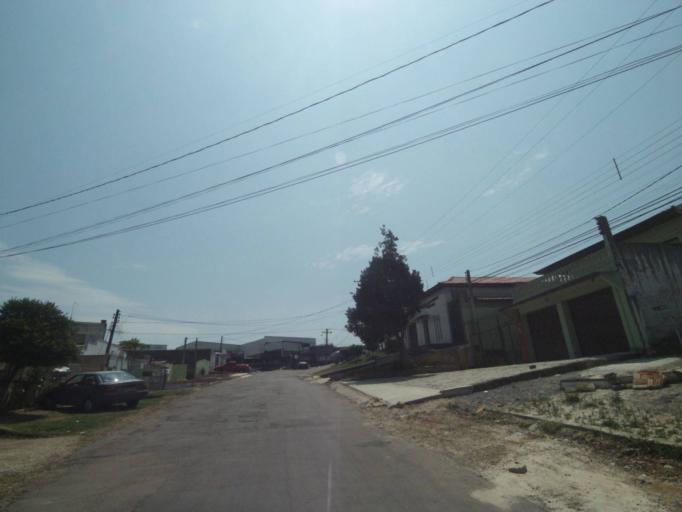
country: BR
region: Parana
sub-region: Curitiba
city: Curitiba
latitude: -25.4793
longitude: -49.3128
